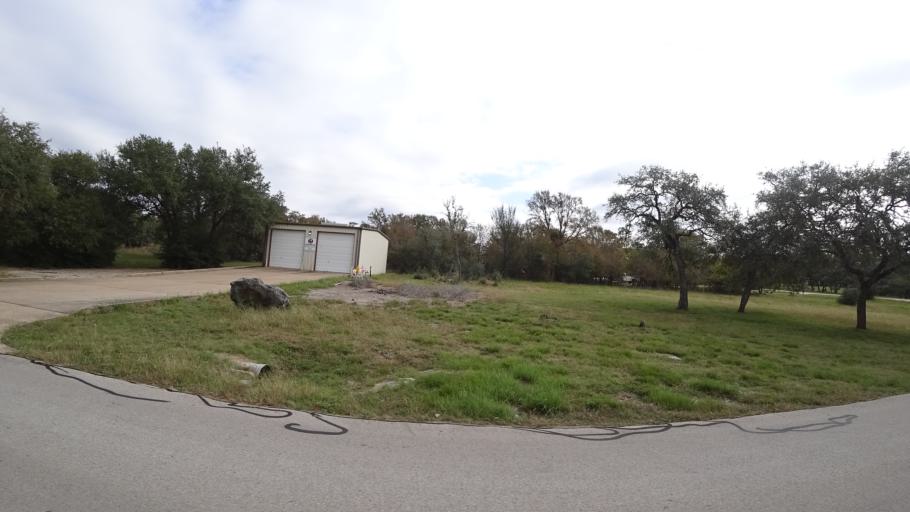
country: US
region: Texas
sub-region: Travis County
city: Shady Hollow
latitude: 30.1368
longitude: -97.8935
